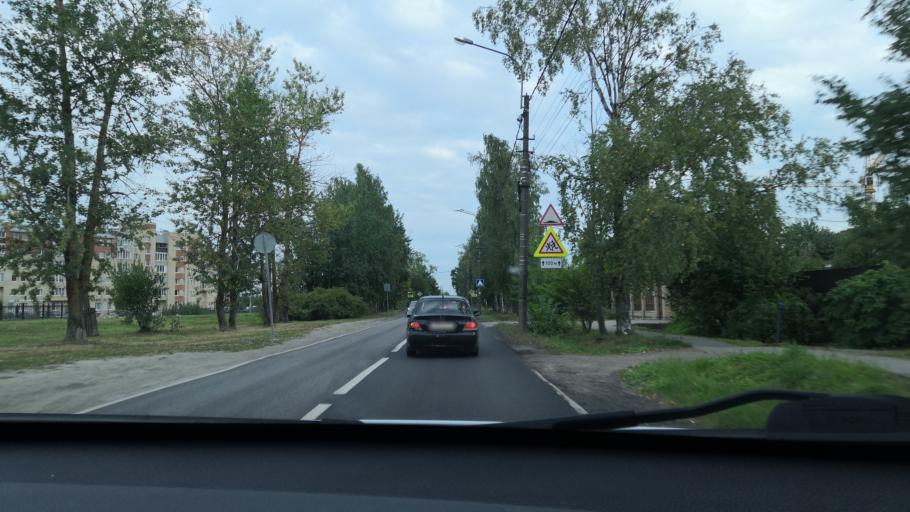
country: RU
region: St.-Petersburg
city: Pushkin
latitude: 59.6977
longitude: 30.4110
